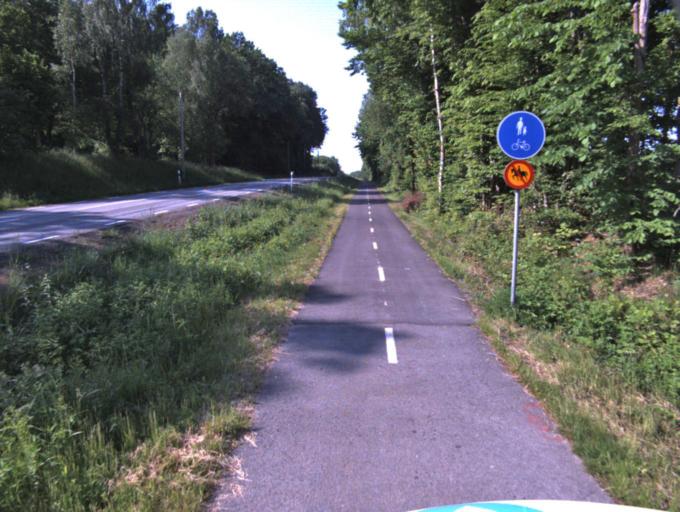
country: SE
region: Skane
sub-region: Kristianstads Kommun
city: Tollarp
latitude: 56.1574
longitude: 14.2696
